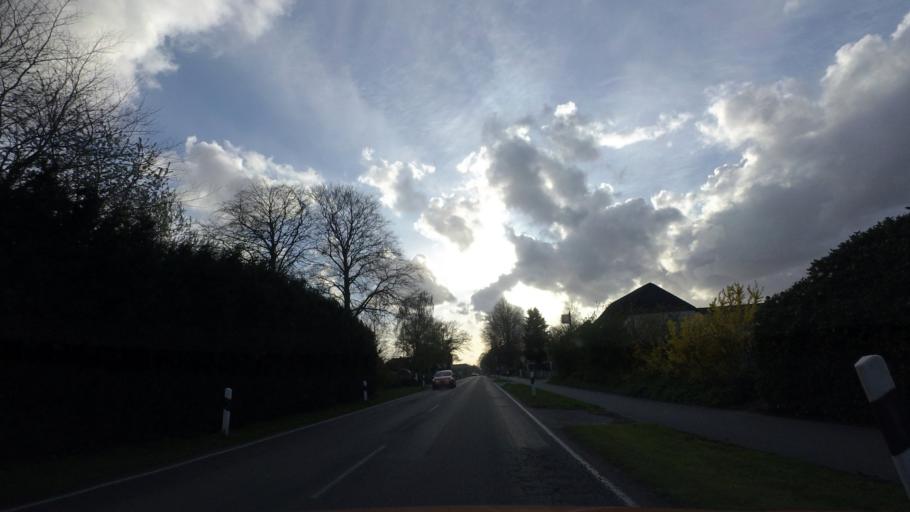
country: DE
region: Lower Saxony
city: Edewecht
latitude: 53.1222
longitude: 8.0338
